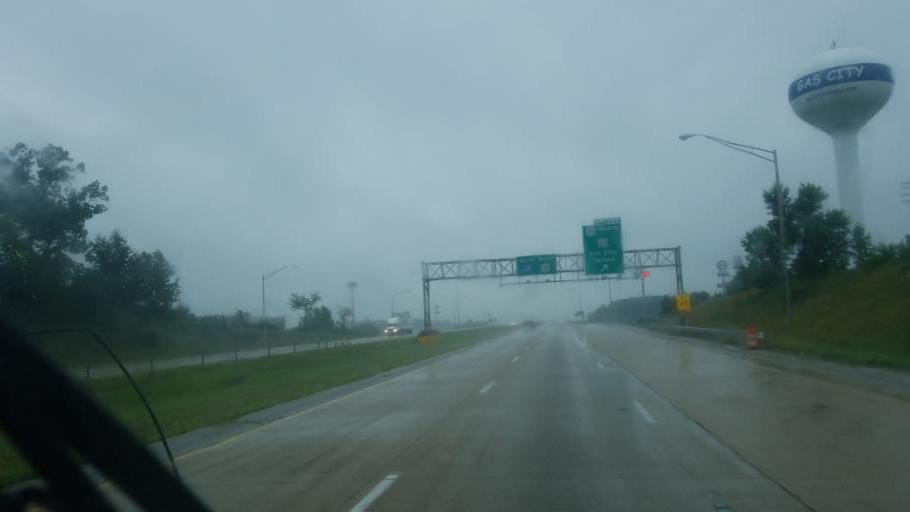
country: US
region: Indiana
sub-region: Grant County
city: Upland
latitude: 40.4848
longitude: -85.5493
